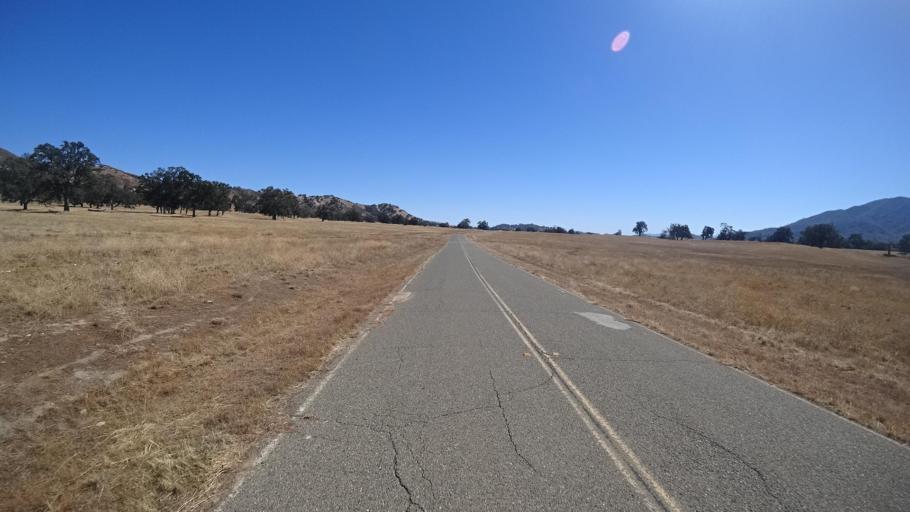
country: US
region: California
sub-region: Monterey County
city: King City
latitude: 35.9711
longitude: -121.3195
